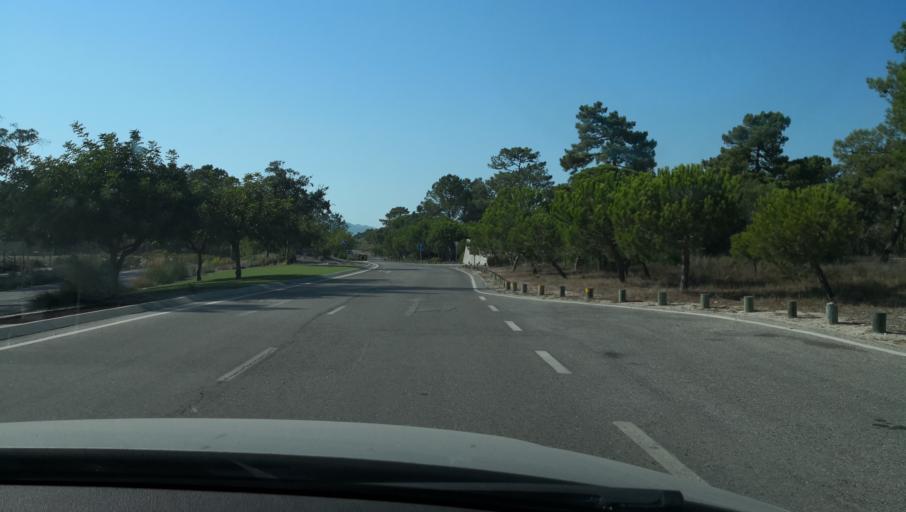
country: PT
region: Setubal
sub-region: Setubal
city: Setubal
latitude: 38.4660
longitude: -8.8740
